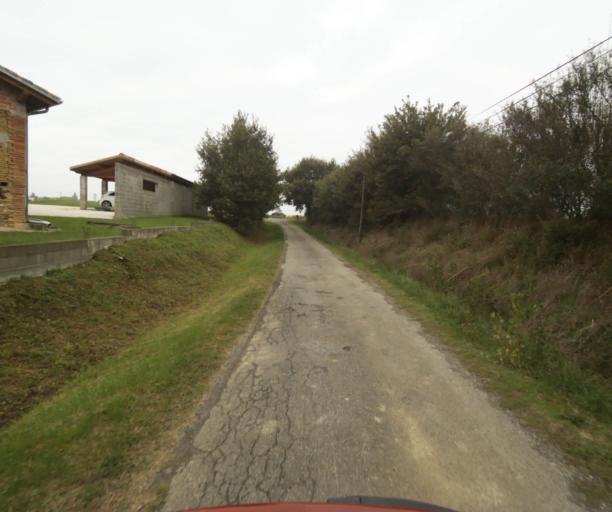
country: FR
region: Midi-Pyrenees
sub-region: Departement du Tarn-et-Garonne
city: Verdun-sur-Garonne
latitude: 43.8031
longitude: 1.2270
